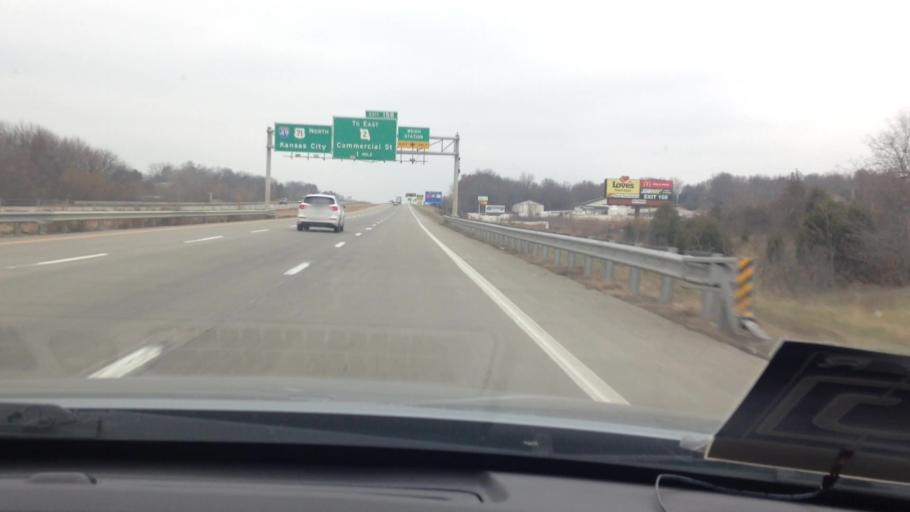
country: US
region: Missouri
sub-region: Cass County
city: Harrisonville
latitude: 38.6206
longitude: -94.3487
